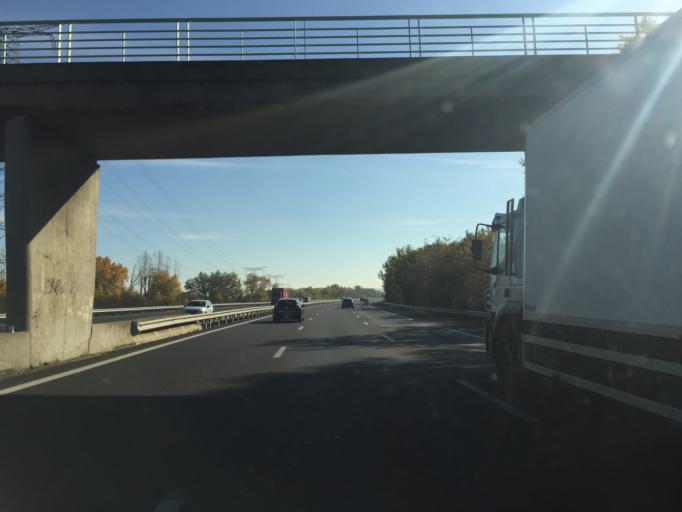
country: FR
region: Provence-Alpes-Cote d'Azur
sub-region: Departement des Bouches-du-Rhone
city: Cabannes
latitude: 43.8507
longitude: 4.9873
